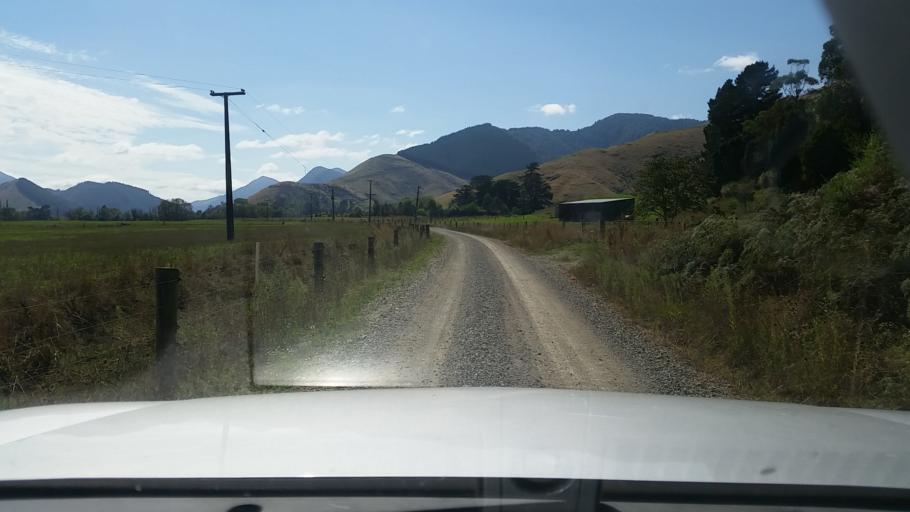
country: NZ
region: Nelson
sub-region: Nelson City
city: Nelson
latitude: -41.2605
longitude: 173.5807
